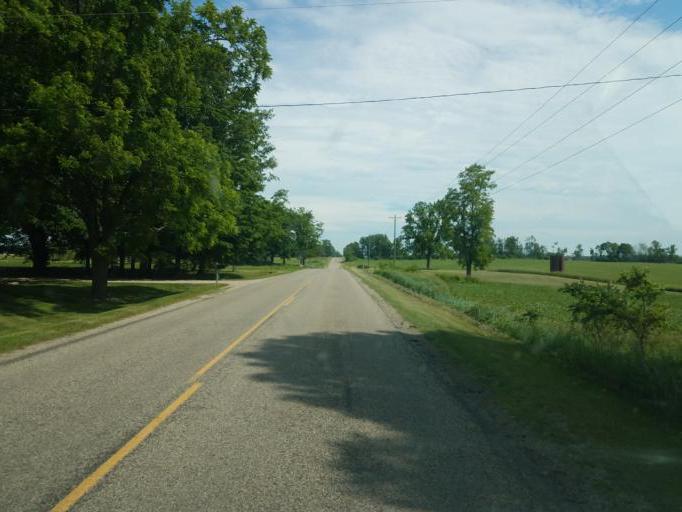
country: US
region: Michigan
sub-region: Barry County
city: Nashville
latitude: 42.6725
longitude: -85.0343
